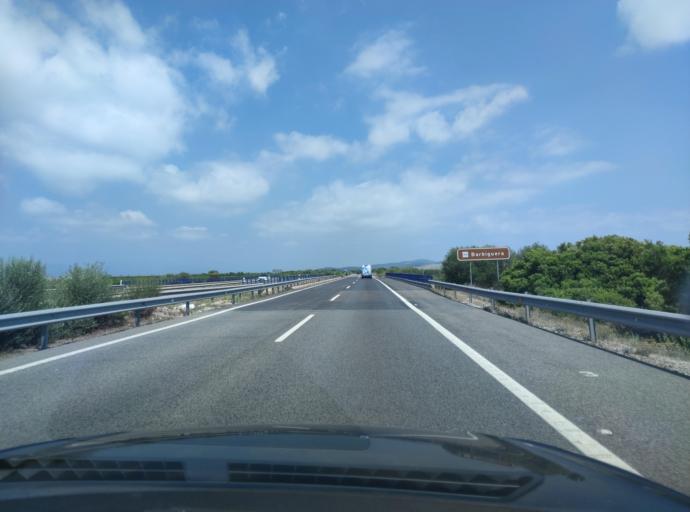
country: ES
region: Catalonia
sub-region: Provincia de Tarragona
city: Alcanar
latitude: 40.5351
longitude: 0.4189
